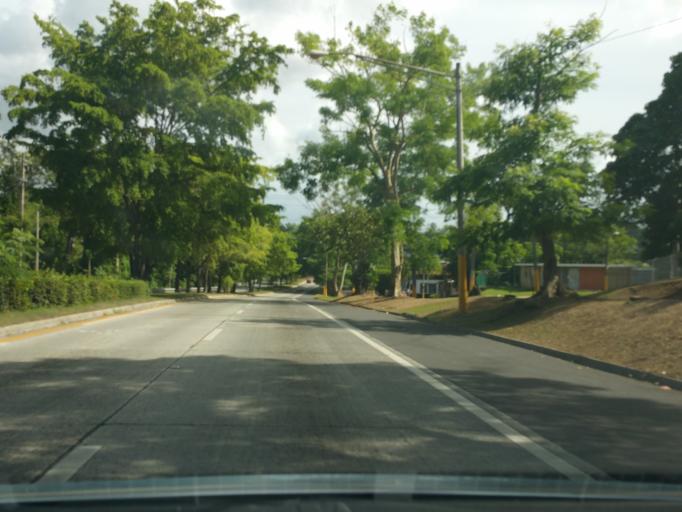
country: PR
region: Trujillo Alto
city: Trujillo Alto
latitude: 18.3861
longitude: -66.0291
